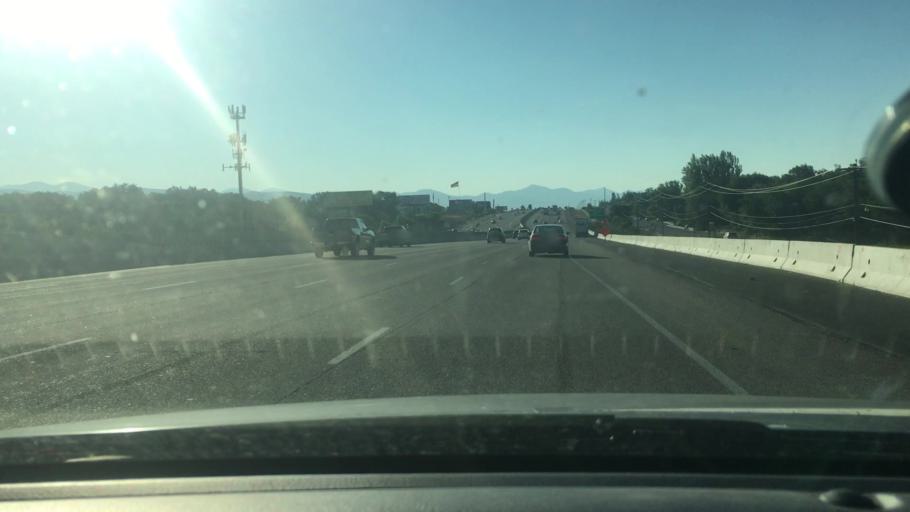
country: US
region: Utah
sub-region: Utah County
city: Lehi
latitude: 40.4001
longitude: -111.8478
